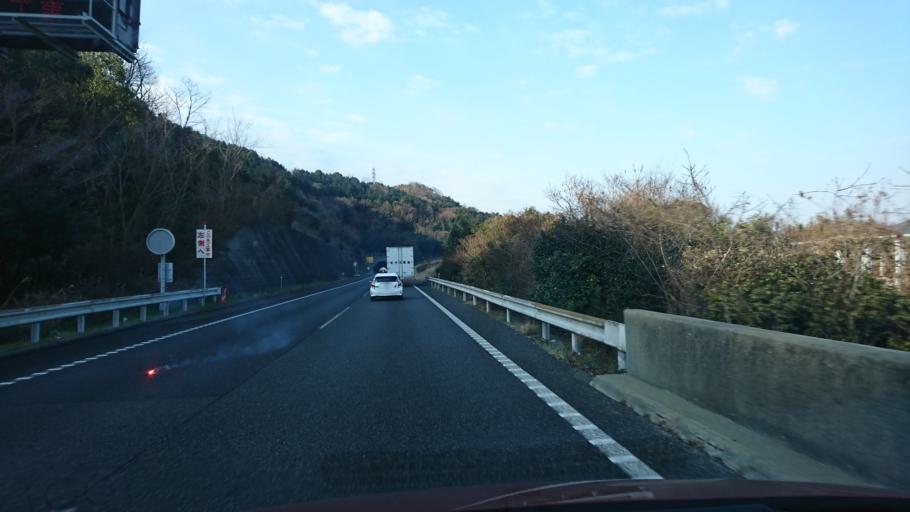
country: JP
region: Hyogo
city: Tatsunocho-tominaga
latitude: 34.8604
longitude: 134.5750
